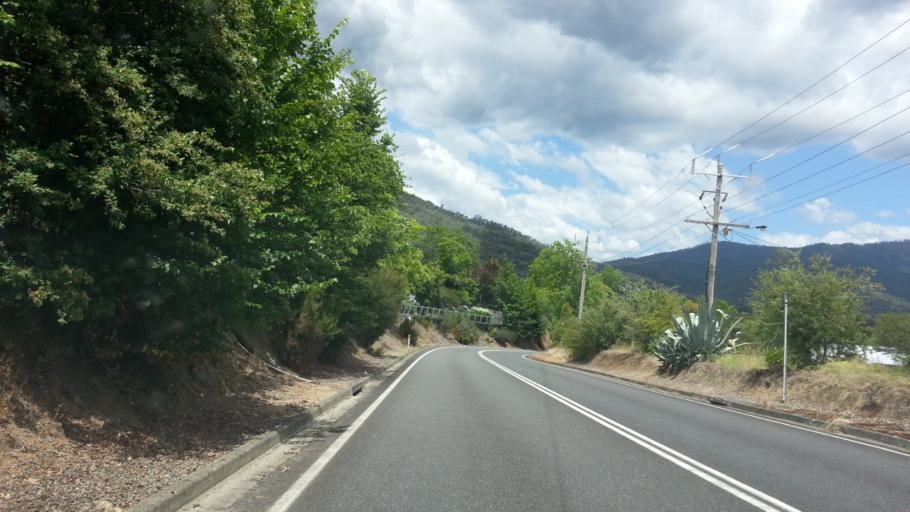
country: AU
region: Victoria
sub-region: Alpine
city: Mount Beauty
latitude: -36.7434
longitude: 147.1738
